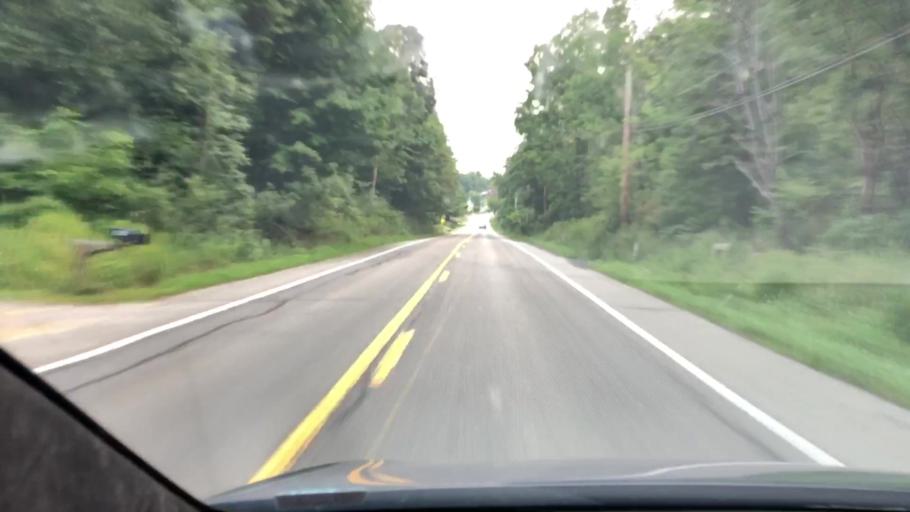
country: US
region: Pennsylvania
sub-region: Mercer County
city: Grove City
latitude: 41.1814
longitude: -79.9788
